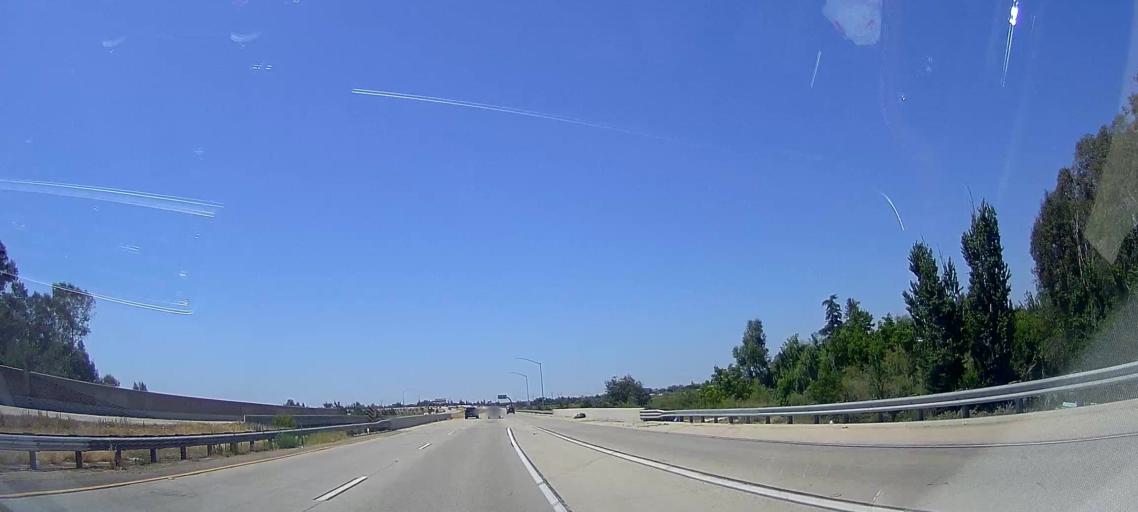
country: US
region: California
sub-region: Fresno County
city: Sunnyside
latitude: 36.7432
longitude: -119.6688
